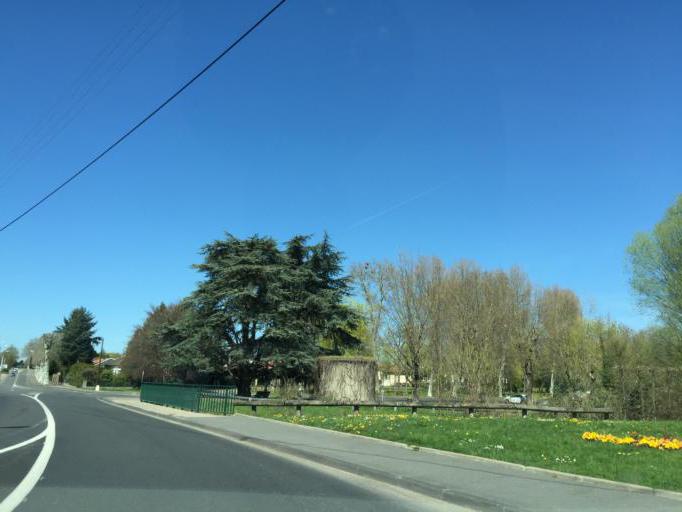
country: FR
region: Rhone-Alpes
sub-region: Departement de la Loire
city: Feurs
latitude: 45.7479
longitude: 4.2220
